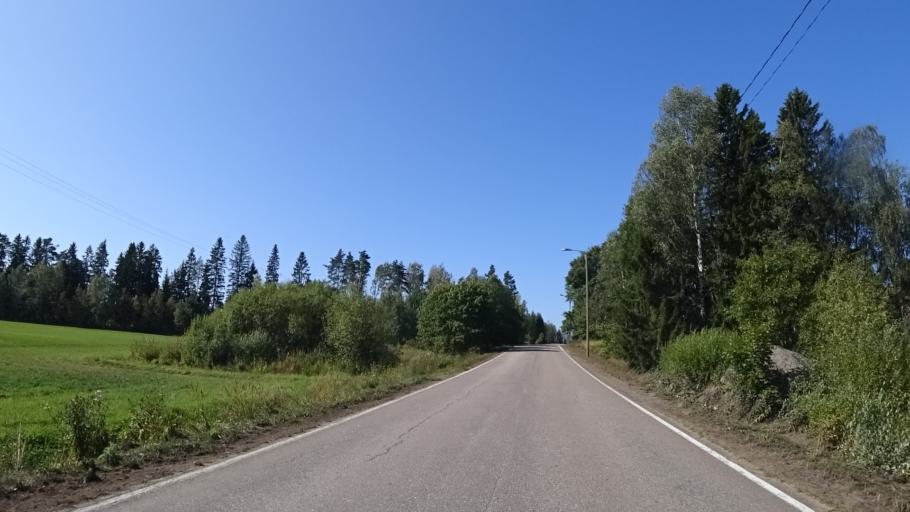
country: FI
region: Kymenlaakso
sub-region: Kotka-Hamina
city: Virolahti
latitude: 60.5150
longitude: 27.4459
